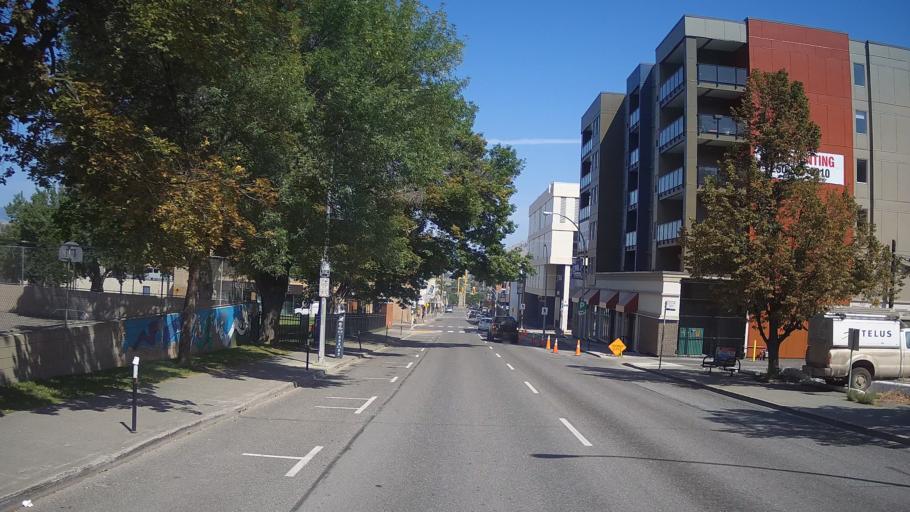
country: CA
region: British Columbia
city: Kamloops
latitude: 50.6733
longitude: -120.3345
